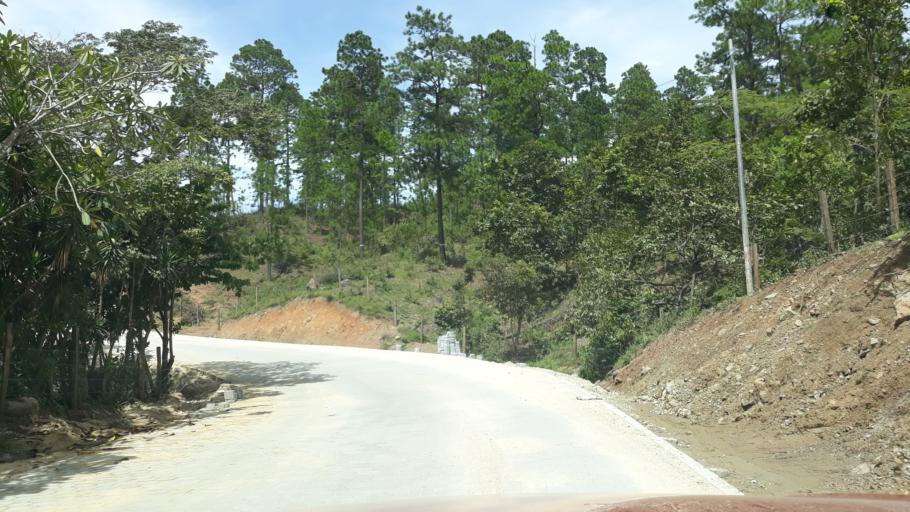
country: HN
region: El Paraiso
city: Santa Cruz
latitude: 13.7577
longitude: -86.6311
